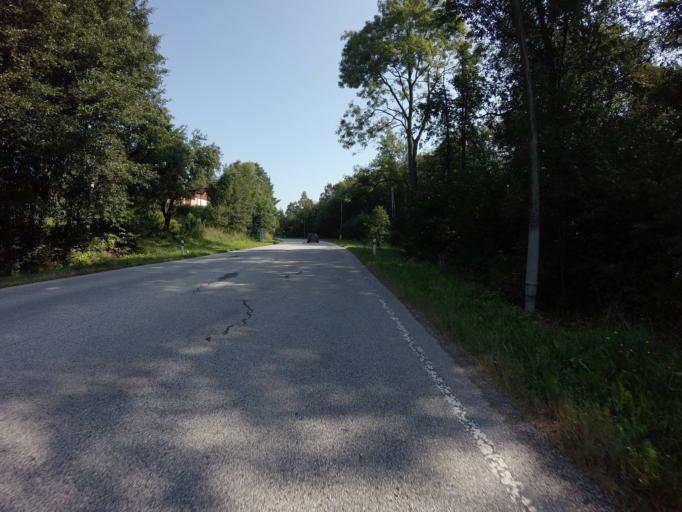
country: CZ
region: Jihocesky
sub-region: Okres Cesky Krumlov
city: Vyssi Brod
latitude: 48.5818
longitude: 14.3199
